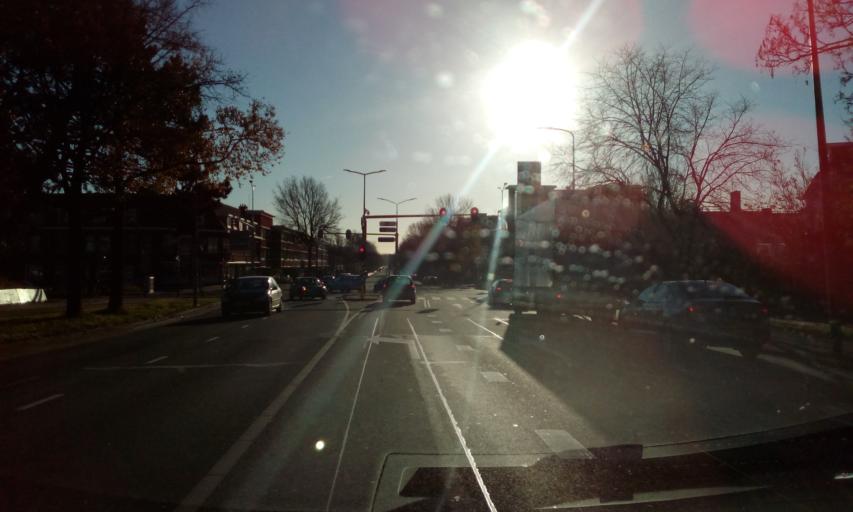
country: NL
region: South Holland
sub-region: Gemeente Den Haag
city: The Hague
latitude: 52.1045
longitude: 4.3166
